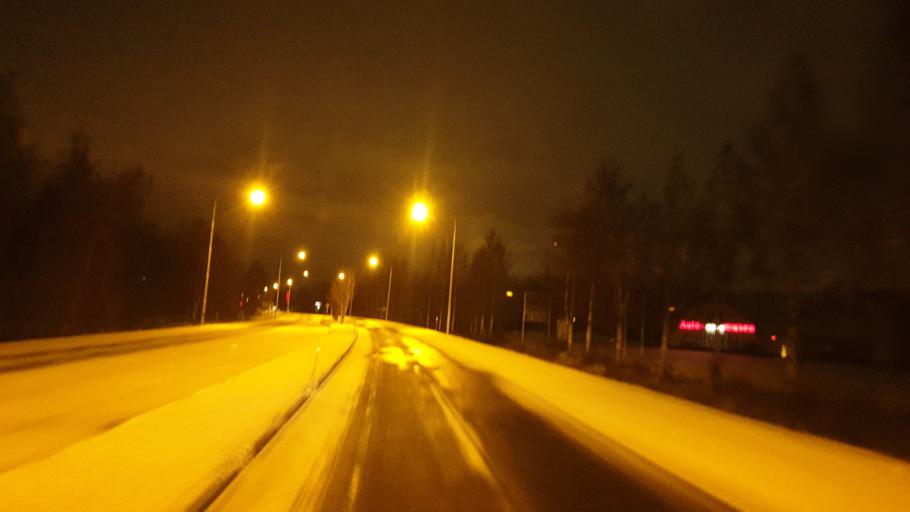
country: FI
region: Northern Ostrobothnia
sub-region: Oulu
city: Kempele
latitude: 64.9626
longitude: 25.5021
